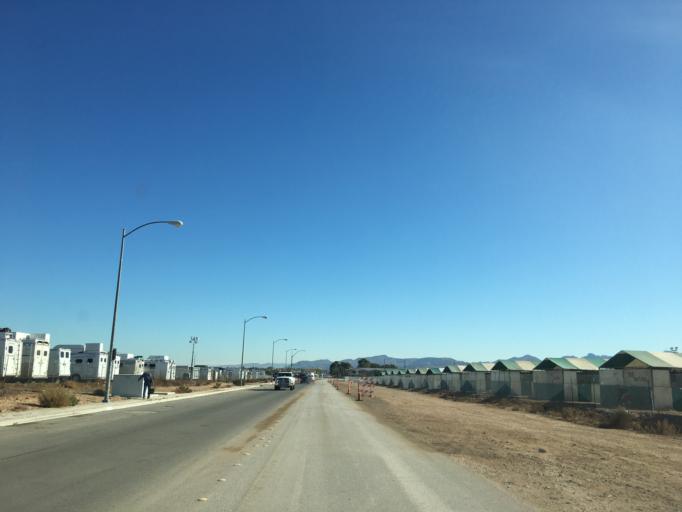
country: US
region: Nevada
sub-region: Clark County
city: Enterprise
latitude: 36.0064
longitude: -115.1755
